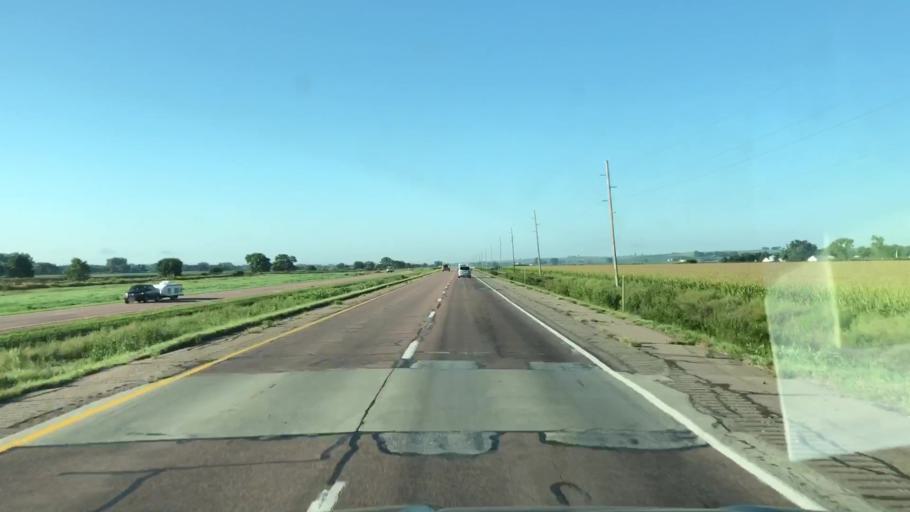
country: US
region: Iowa
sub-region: Plymouth County
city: Le Mars
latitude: 42.7064
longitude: -96.2548
